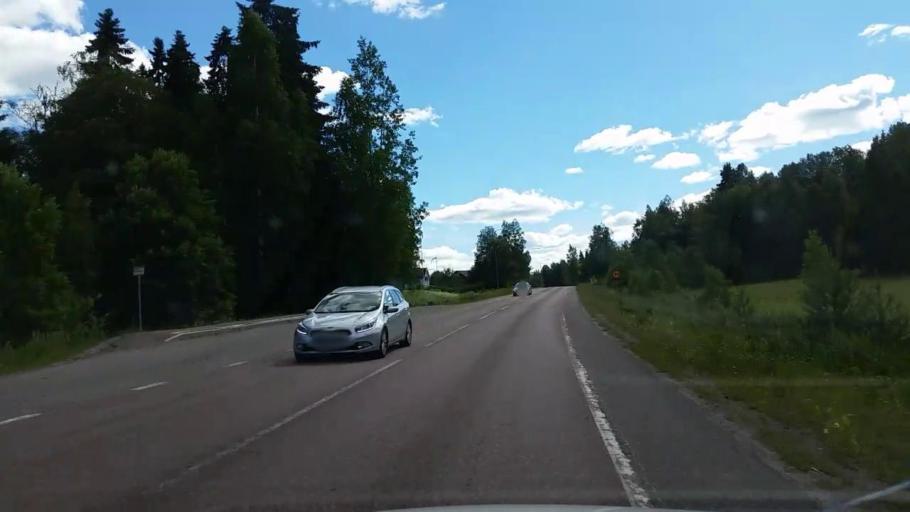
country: SE
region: Dalarna
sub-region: Faluns Kommun
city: Svardsjo
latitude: 60.8409
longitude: 15.7619
